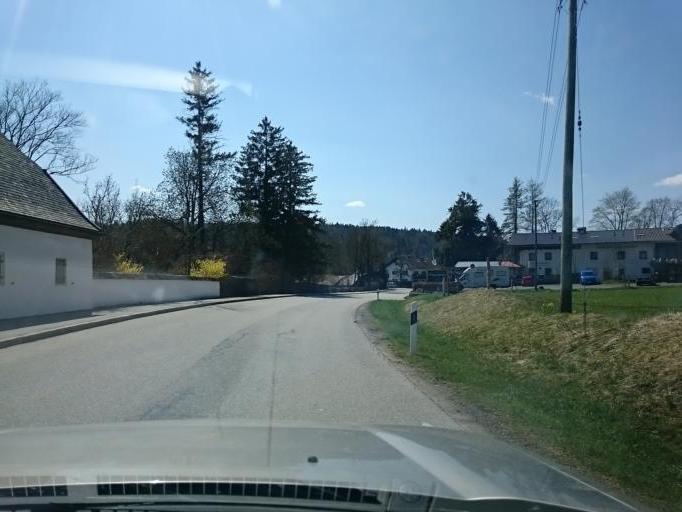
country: DE
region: Bavaria
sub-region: Upper Bavaria
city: Schlehdorf
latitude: 47.5908
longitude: 11.3172
